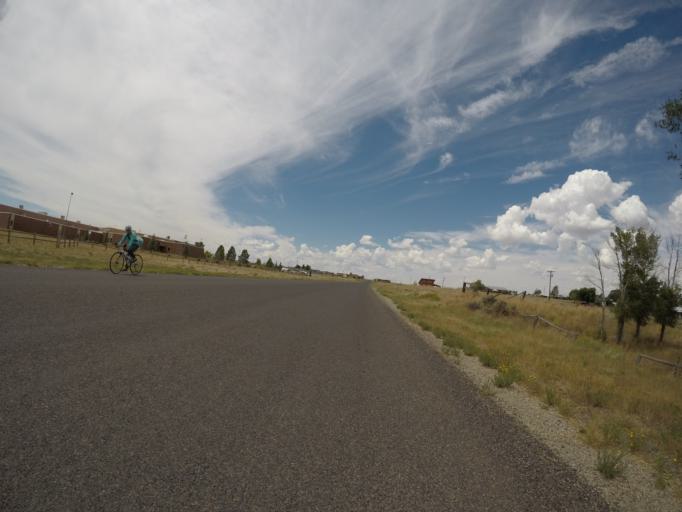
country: US
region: Wyoming
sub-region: Carbon County
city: Saratoga
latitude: 41.4529
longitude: -106.8177
